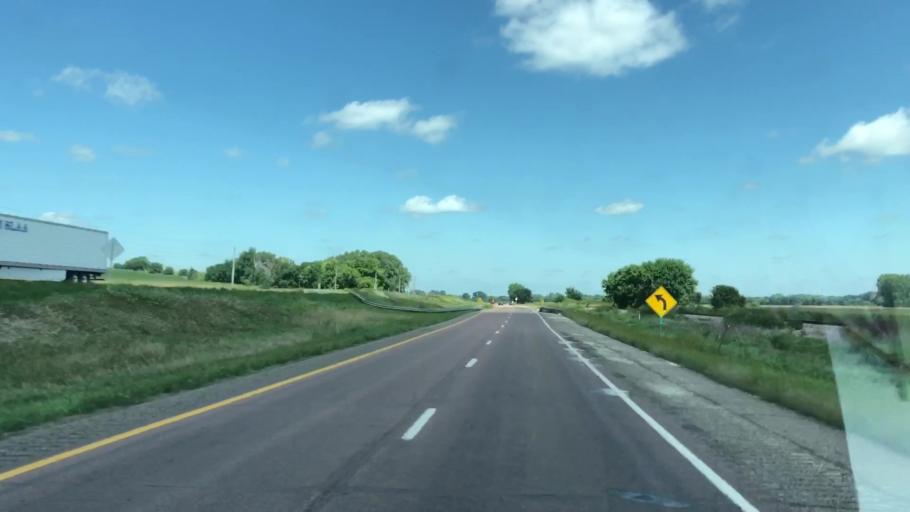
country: US
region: Iowa
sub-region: Woodbury County
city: Sioux City
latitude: 42.5797
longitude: -96.3134
